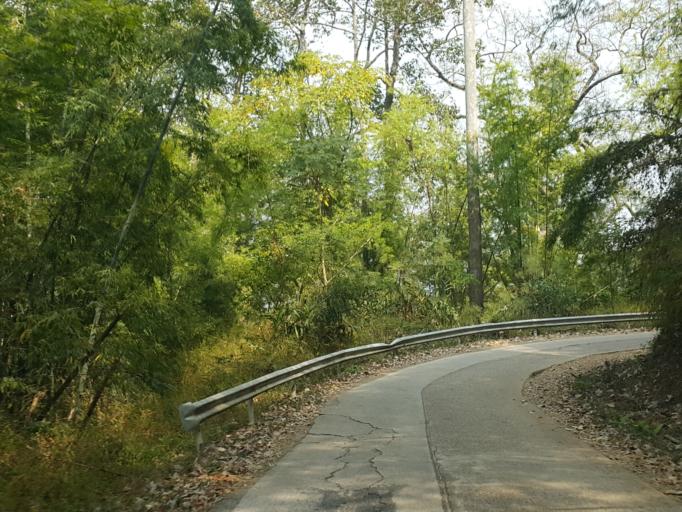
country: TH
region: Chiang Mai
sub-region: Amphoe Chiang Dao
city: Chiang Dao
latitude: 19.4120
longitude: 98.8699
